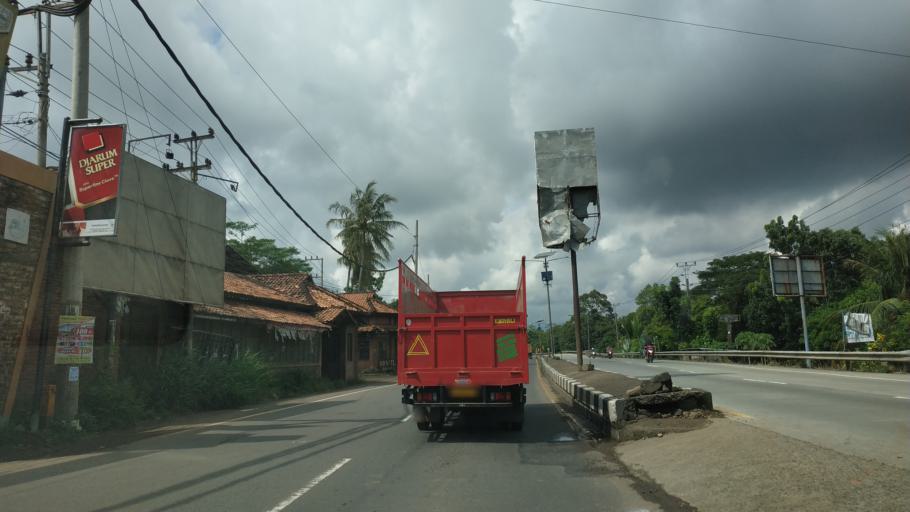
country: ID
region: Central Java
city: Pekalongan
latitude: -6.9371
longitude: 109.7746
